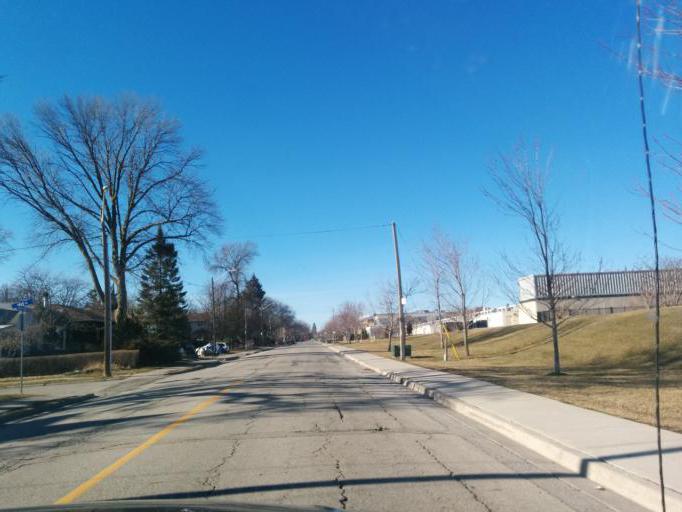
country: CA
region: Ontario
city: Etobicoke
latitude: 43.5919
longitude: -79.5196
